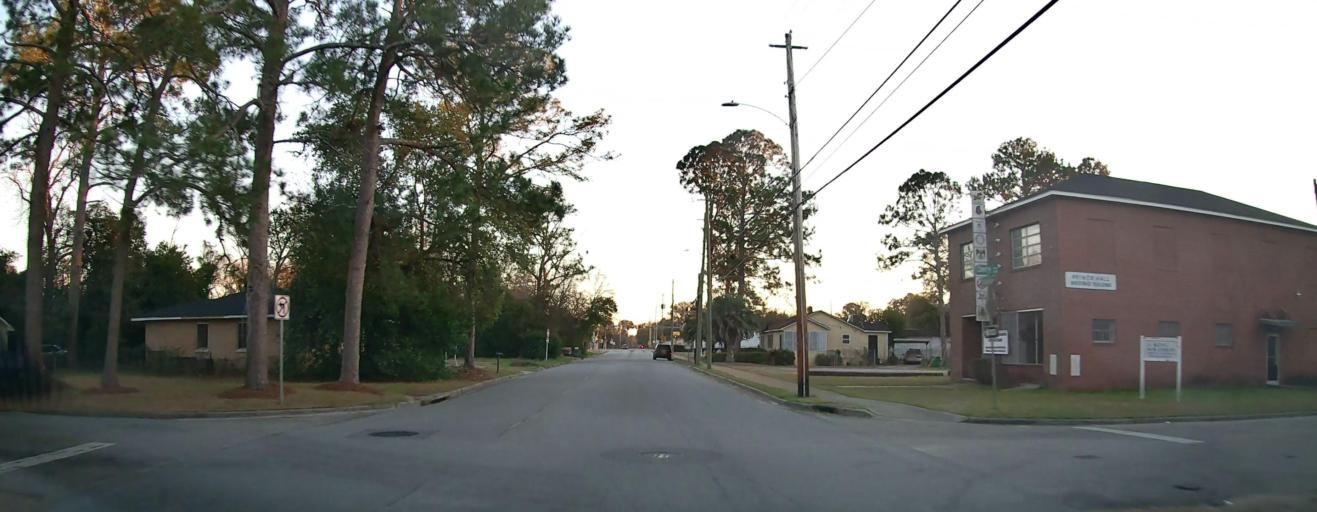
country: US
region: Georgia
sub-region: Dougherty County
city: Albany
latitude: 31.5655
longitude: -84.1619
